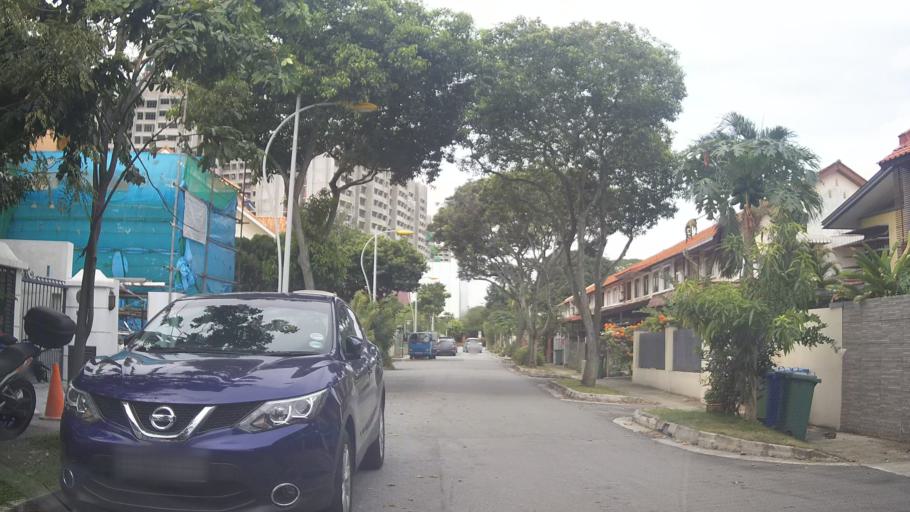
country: SG
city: Singapore
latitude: 1.3317
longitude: 103.8731
